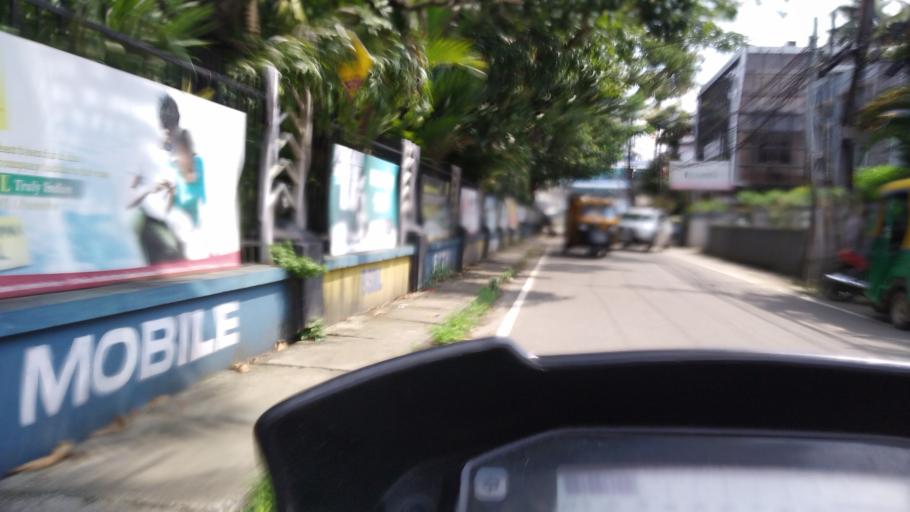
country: IN
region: Kerala
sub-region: Ernakulam
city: Cochin
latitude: 9.9660
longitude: 76.2902
